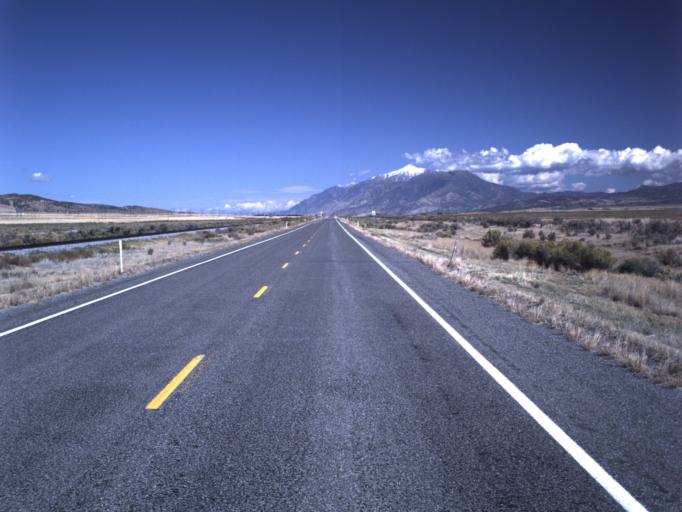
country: US
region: Utah
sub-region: Juab County
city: Nephi
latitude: 39.5362
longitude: -111.9301
